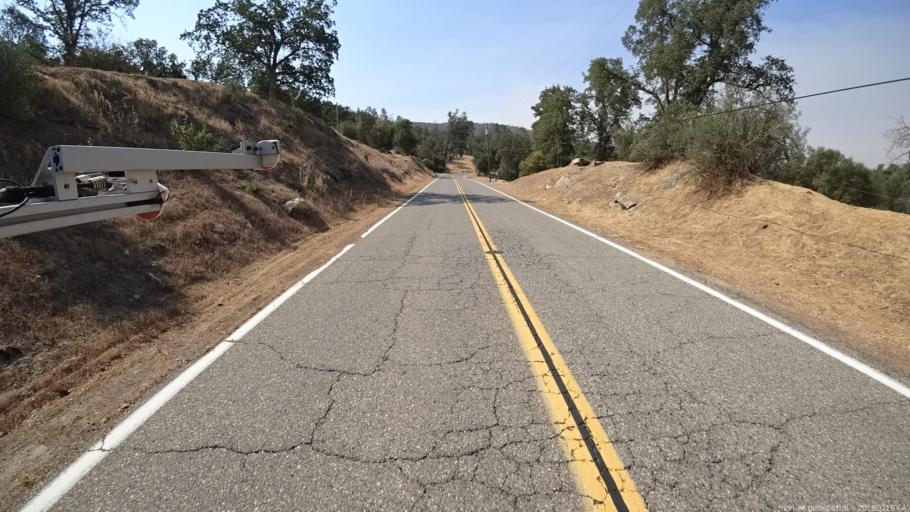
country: US
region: California
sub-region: Madera County
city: Yosemite Lakes
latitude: 37.2053
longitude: -119.7986
